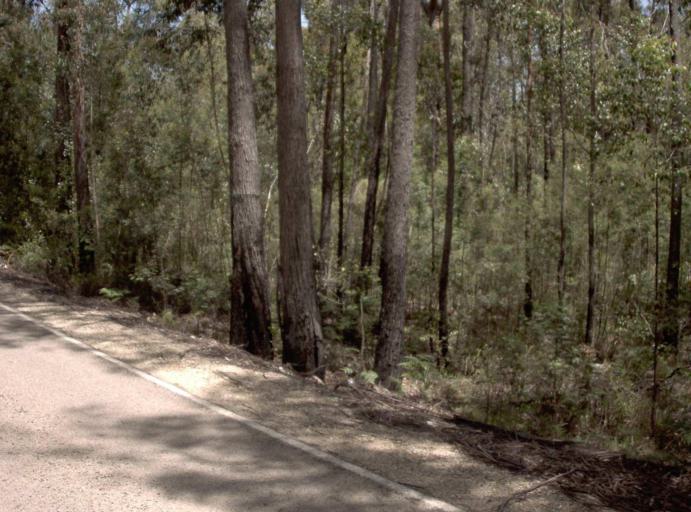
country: AU
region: Victoria
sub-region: East Gippsland
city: Lakes Entrance
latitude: -37.6389
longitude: 147.8963
